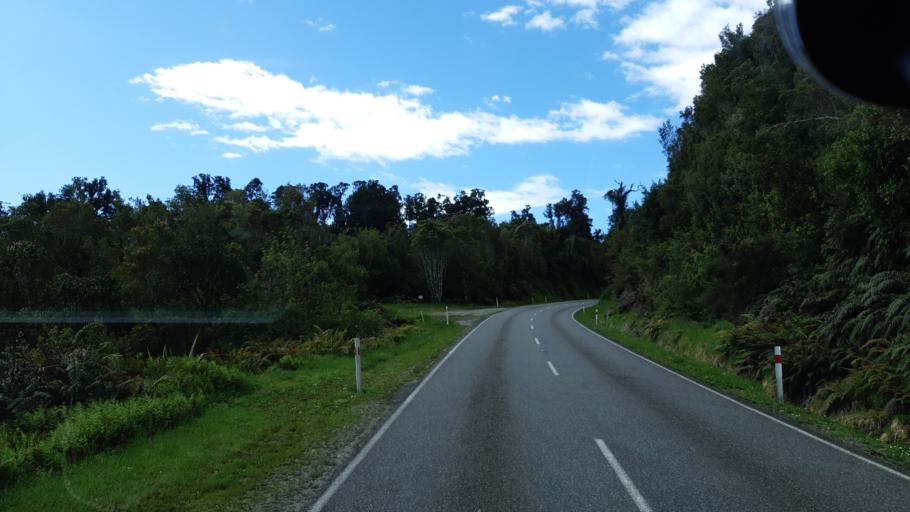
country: NZ
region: West Coast
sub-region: Westland District
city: Hokitika
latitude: -43.0440
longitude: 170.6393
